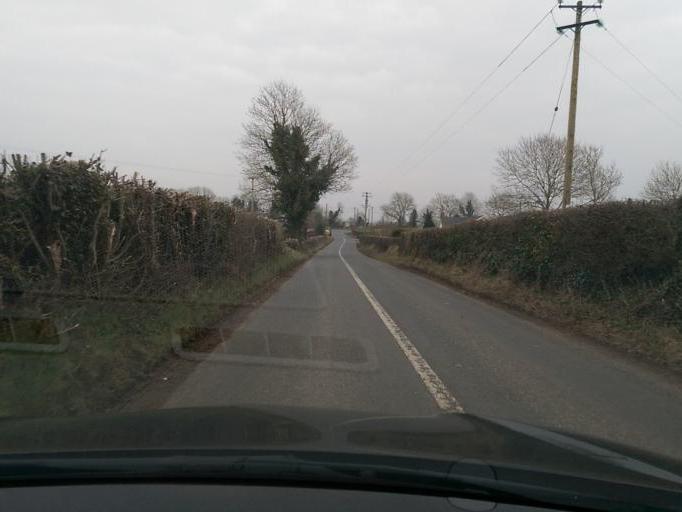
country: IE
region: Leinster
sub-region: An Longfort
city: Longford
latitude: 53.6588
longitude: -7.8247
